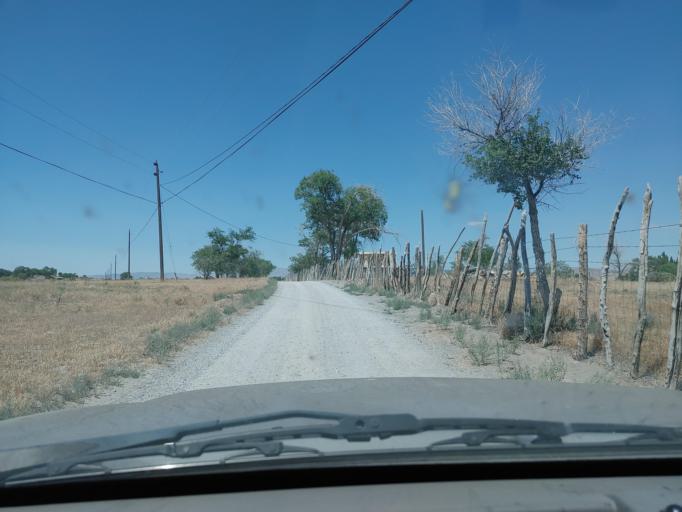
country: US
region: Nevada
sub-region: Humboldt County
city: Winnemucca
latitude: 40.6595
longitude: -118.1339
